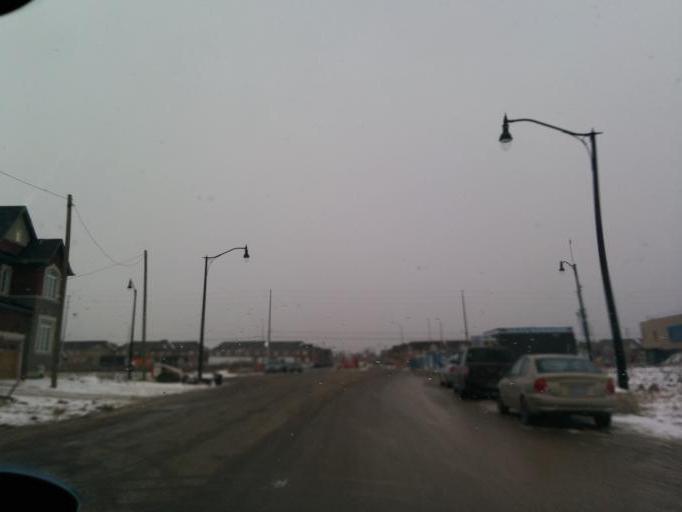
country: CA
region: Ontario
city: Brampton
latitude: 43.6318
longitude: -79.7849
